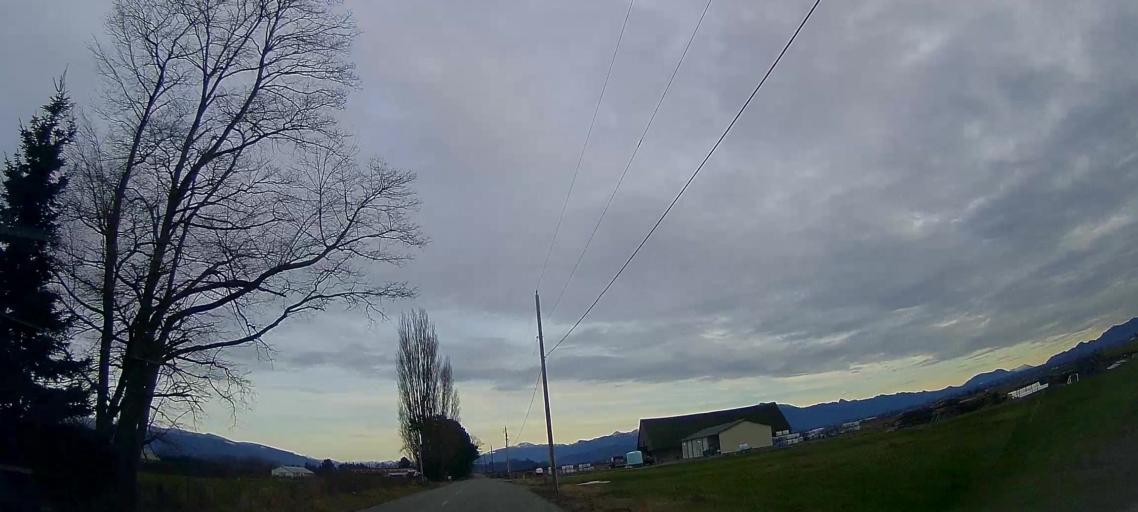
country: US
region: Washington
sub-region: Skagit County
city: Burlington
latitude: 48.5012
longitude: -122.4018
